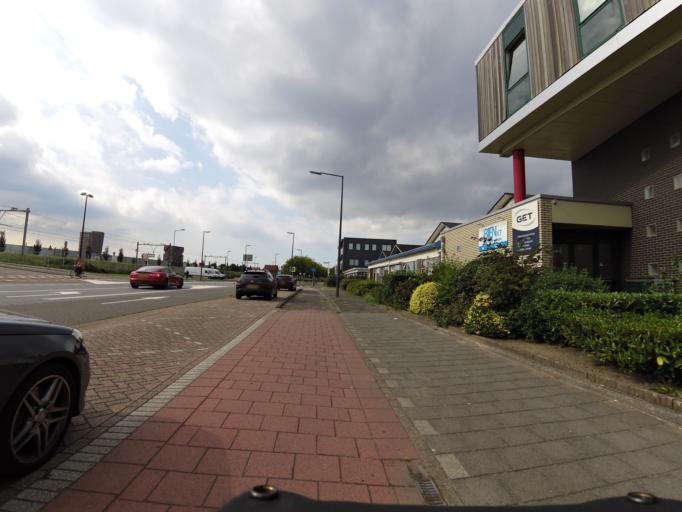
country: NL
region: South Holland
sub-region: Gemeente Maassluis
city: Maassluis
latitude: 51.9195
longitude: 4.2479
